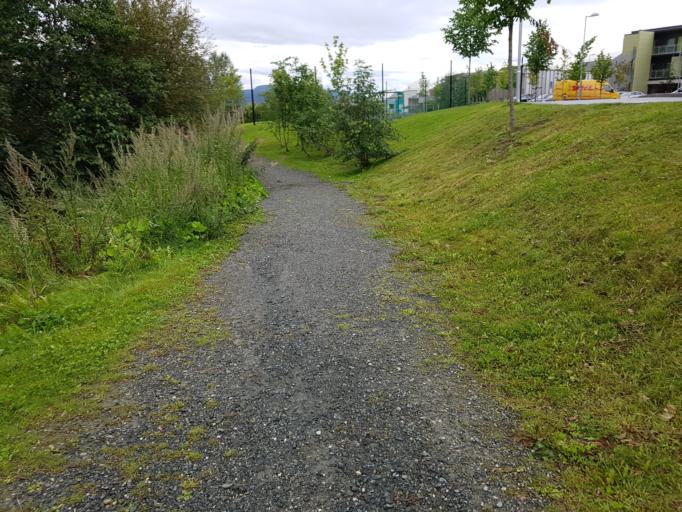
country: NO
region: Sor-Trondelag
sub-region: Trondheim
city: Trondheim
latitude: 63.3908
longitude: 10.4365
